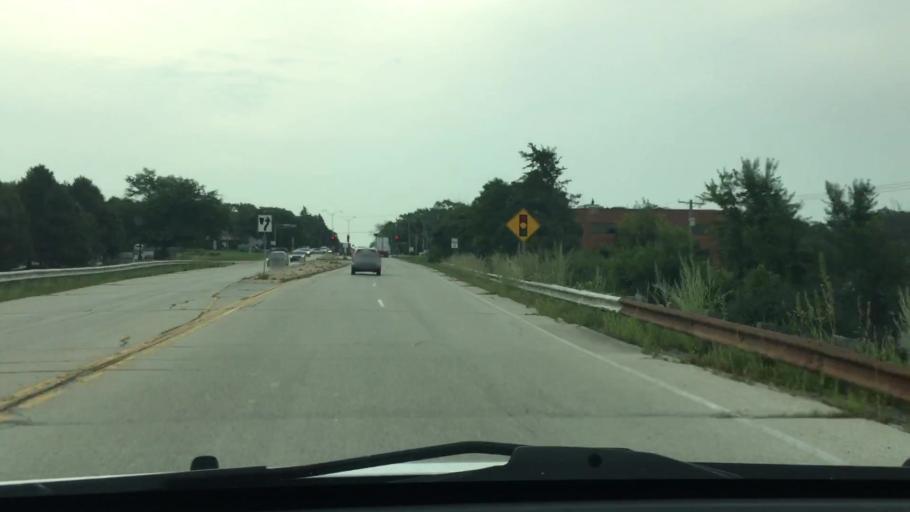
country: US
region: Wisconsin
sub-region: Waukesha County
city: New Berlin
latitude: 42.9954
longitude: -88.1111
